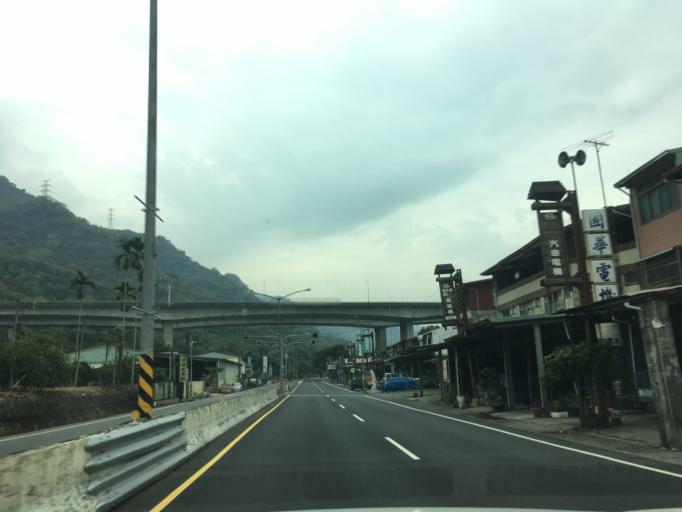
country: TW
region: Taiwan
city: Zhongxing New Village
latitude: 24.0076
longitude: 120.8179
